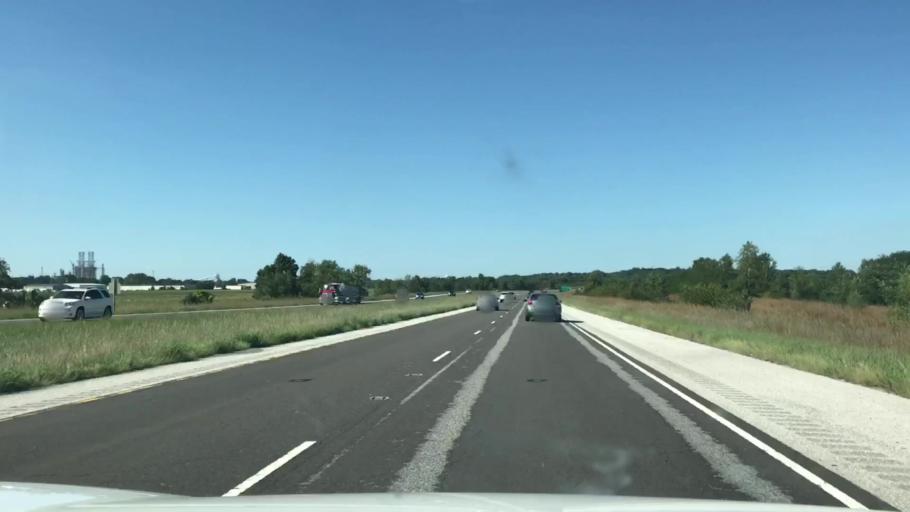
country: US
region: Illinois
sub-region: Madison County
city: South Roxana
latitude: 38.8219
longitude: -90.0427
